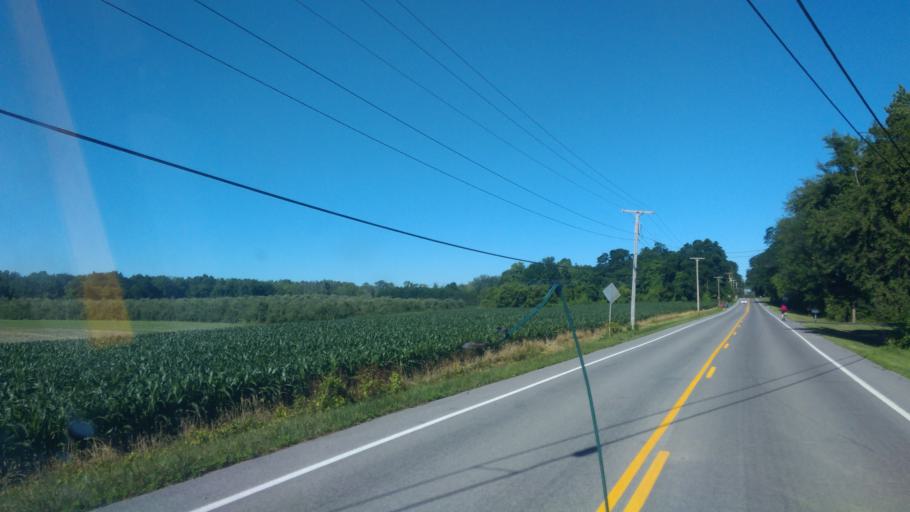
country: US
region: New York
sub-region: Monroe County
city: Webster
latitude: 43.2694
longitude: -77.3782
